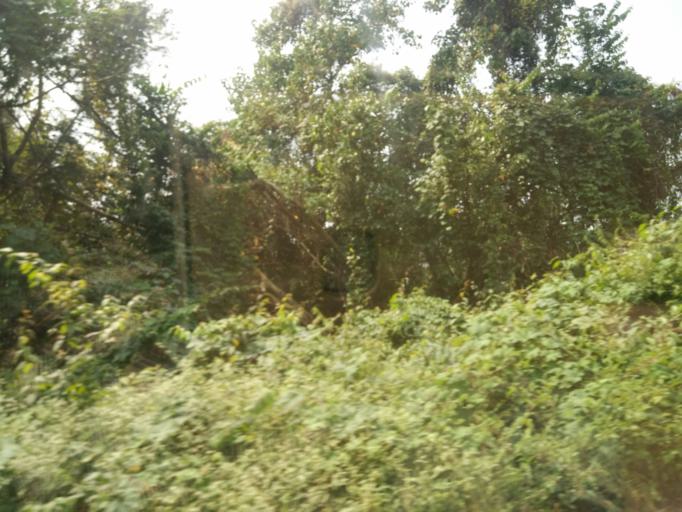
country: IN
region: Goa
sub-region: South Goa
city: Raia
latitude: 15.3160
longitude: 73.9428
